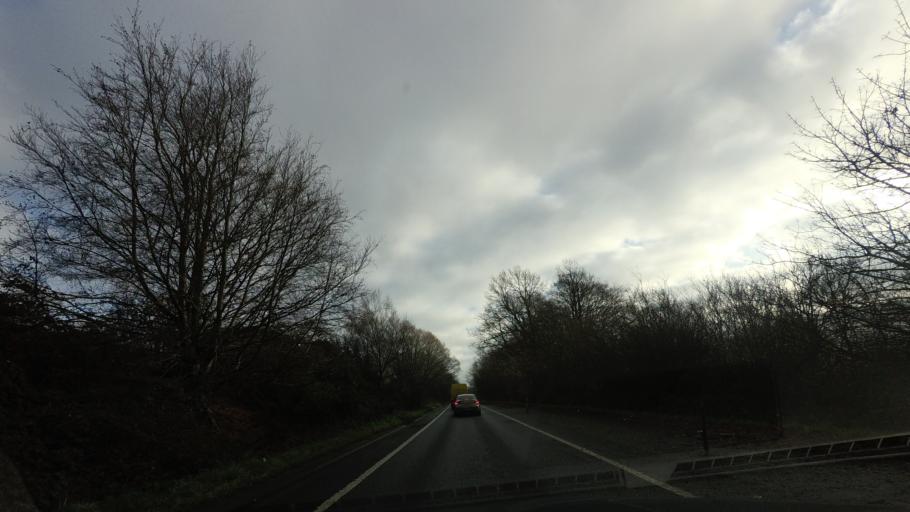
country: GB
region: England
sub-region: Kent
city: Hawkhurst
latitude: 51.0683
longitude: 0.4338
